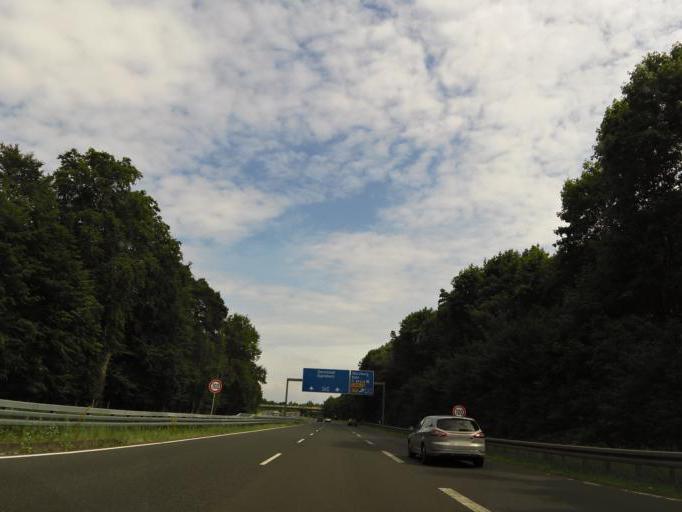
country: DE
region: Hesse
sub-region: Regierungsbezirk Darmstadt
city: Neu Isenburg
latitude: 50.0735
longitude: 8.7214
